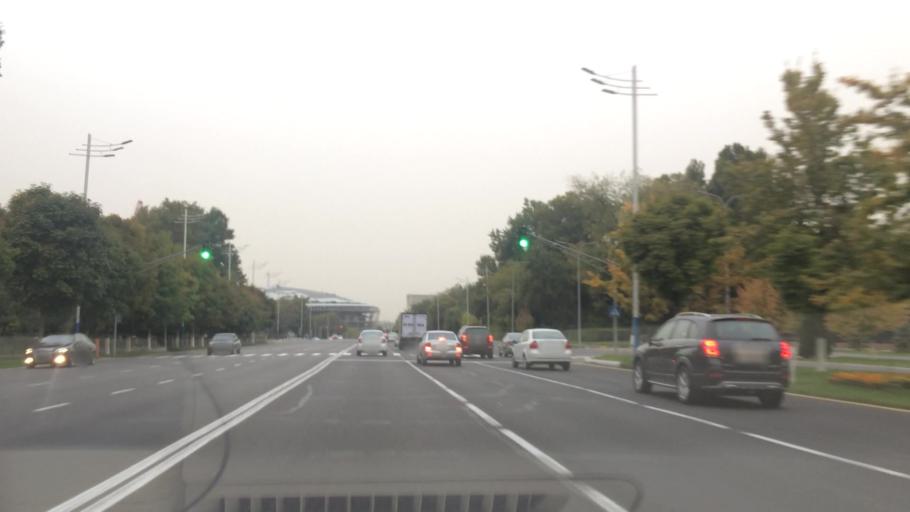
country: UZ
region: Toshkent Shahri
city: Tashkent
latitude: 41.3069
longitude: 69.2592
